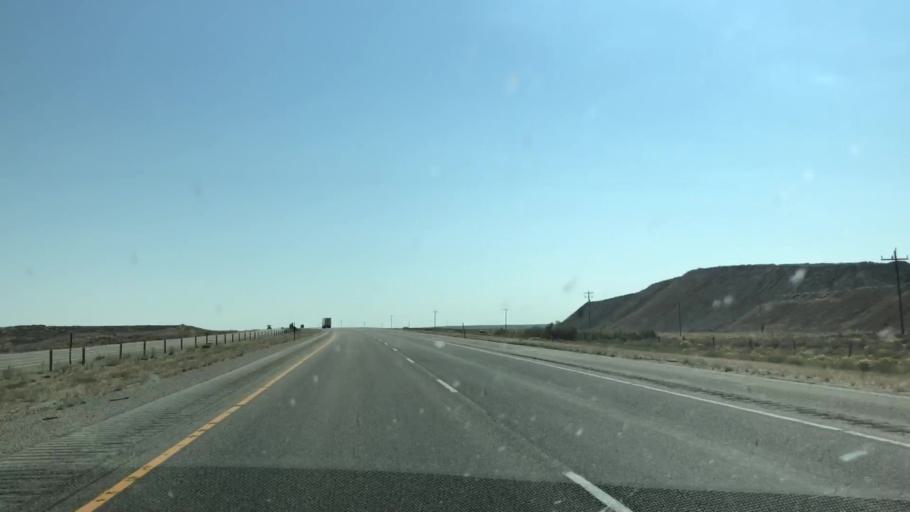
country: US
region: Wyoming
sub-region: Sweetwater County
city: Rock Springs
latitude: 41.6466
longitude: -108.6549
